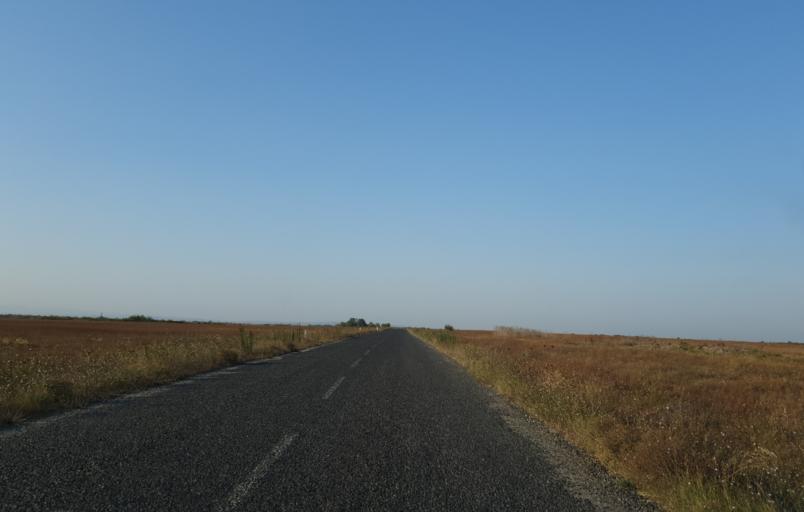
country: TR
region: Tekirdag
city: Beyazkoy
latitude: 41.4064
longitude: 27.7600
